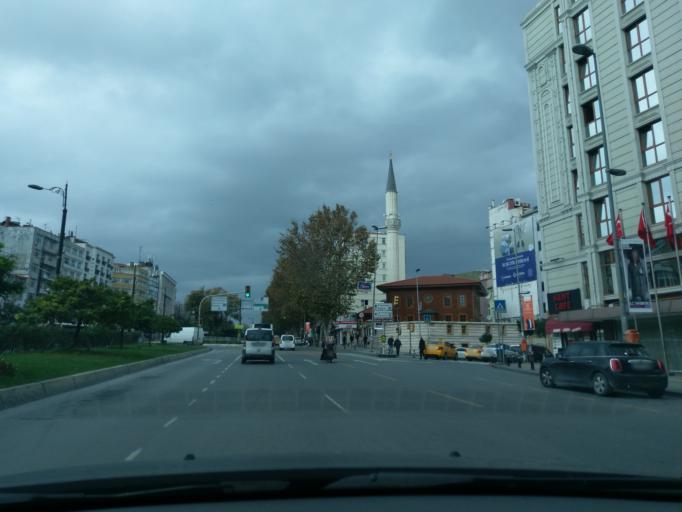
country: TR
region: Istanbul
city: Istanbul
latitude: 41.0123
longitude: 28.9396
